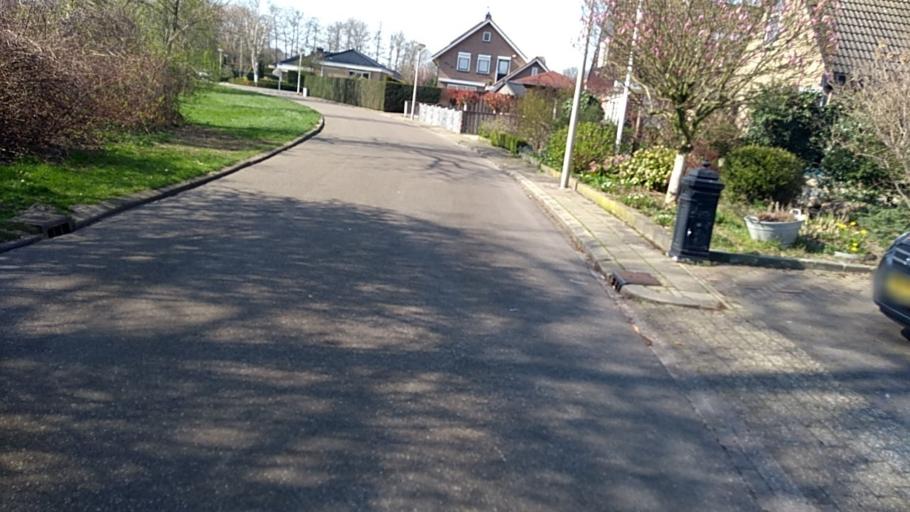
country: NL
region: Overijssel
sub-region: Gemeente Almelo
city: Almelo
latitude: 52.3706
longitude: 6.6927
